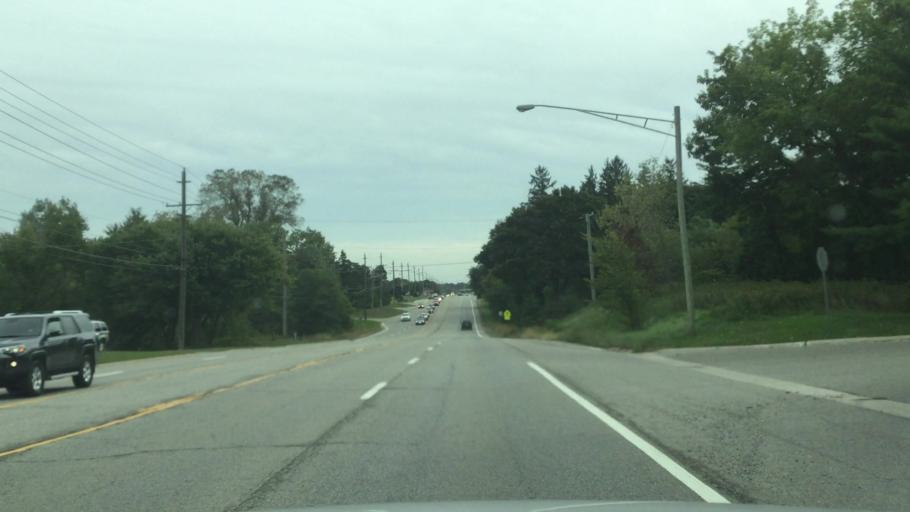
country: US
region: Michigan
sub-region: Oakland County
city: Clarkston
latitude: 42.7479
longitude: -83.4702
